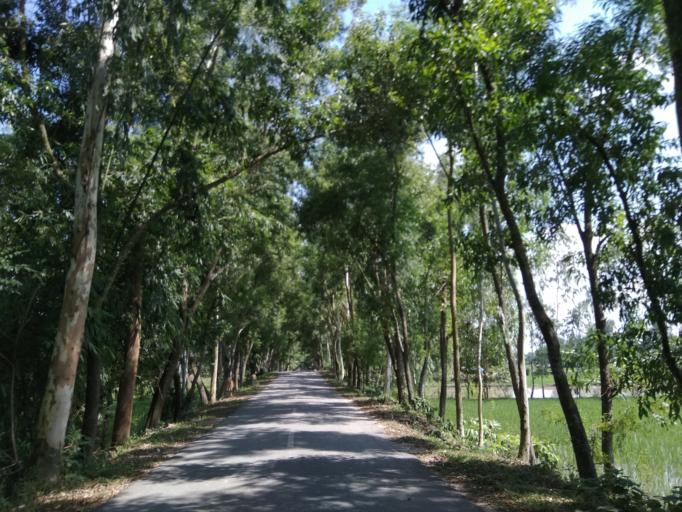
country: IN
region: West Bengal
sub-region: Koch Bihar
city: Haldibari
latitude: 26.1935
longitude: 88.6905
